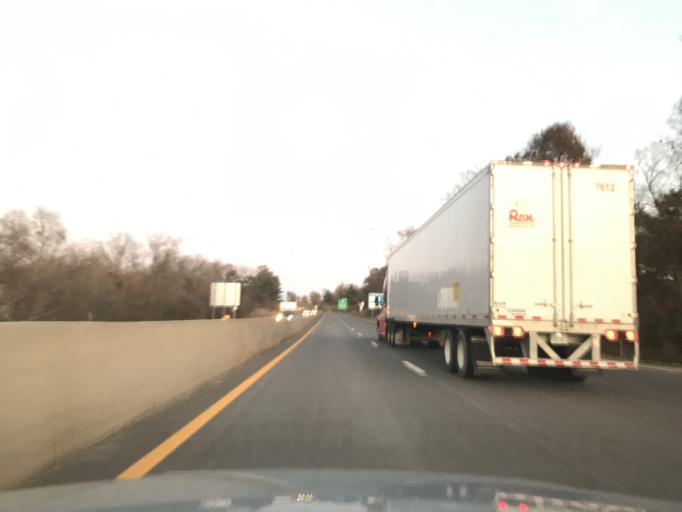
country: US
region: Missouri
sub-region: Marion County
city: Hannibal
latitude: 39.7148
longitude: -91.3884
